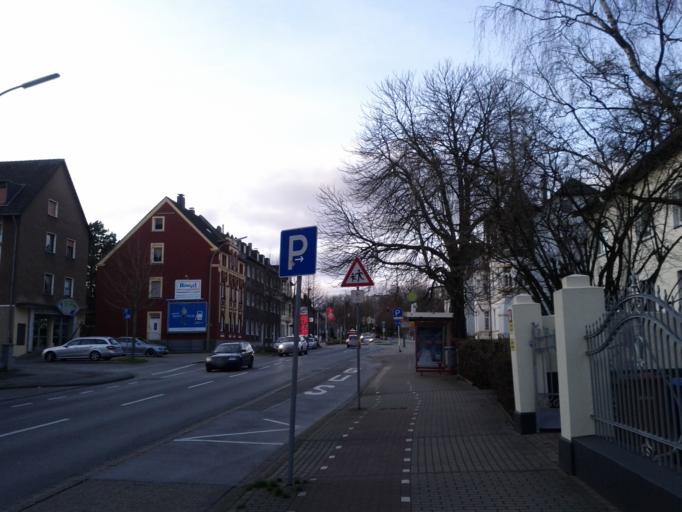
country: DE
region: North Rhine-Westphalia
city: Schwerte
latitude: 51.4916
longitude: 7.5522
